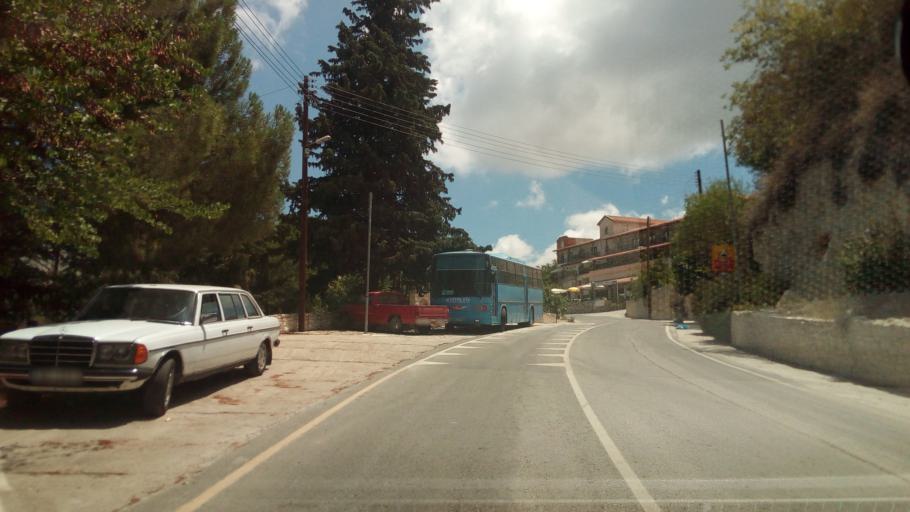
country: CY
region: Pafos
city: Mesogi
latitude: 34.9192
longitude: 32.6287
